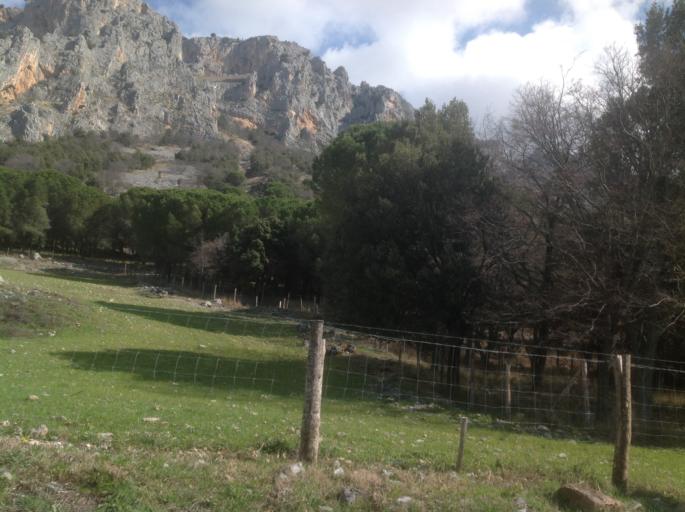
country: IT
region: Calabria
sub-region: Provincia di Cosenza
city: Frascineto
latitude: 39.8317
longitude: 16.2765
